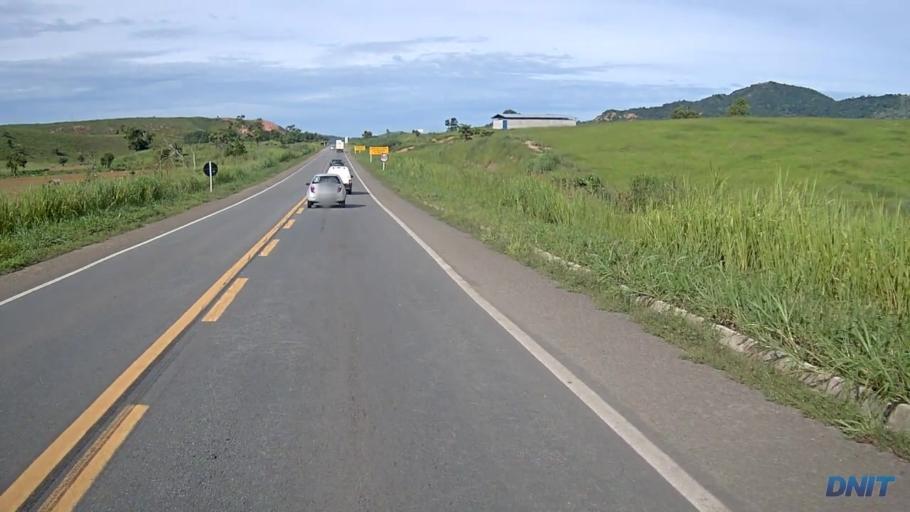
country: BR
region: Minas Gerais
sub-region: Belo Oriente
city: Belo Oriente
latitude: -19.1925
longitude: -42.2761
